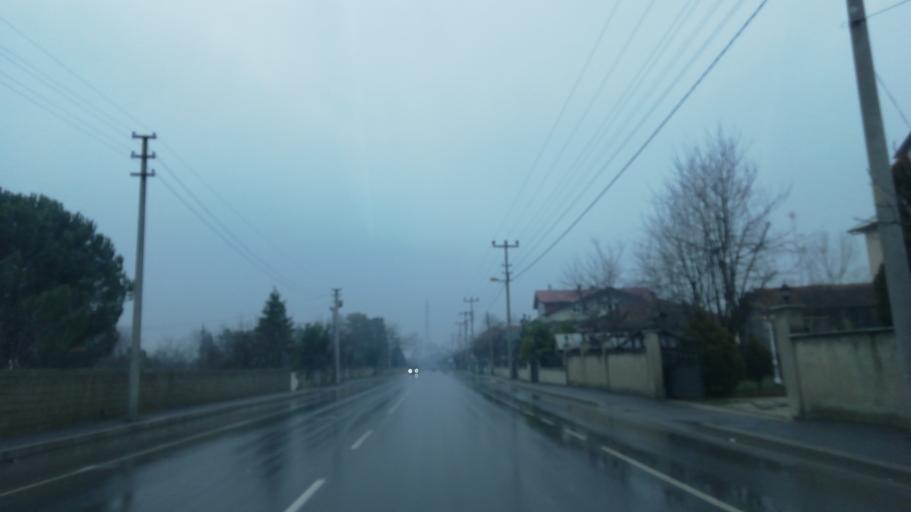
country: TR
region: Sakarya
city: Akyazi
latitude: 40.6494
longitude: 30.6188
